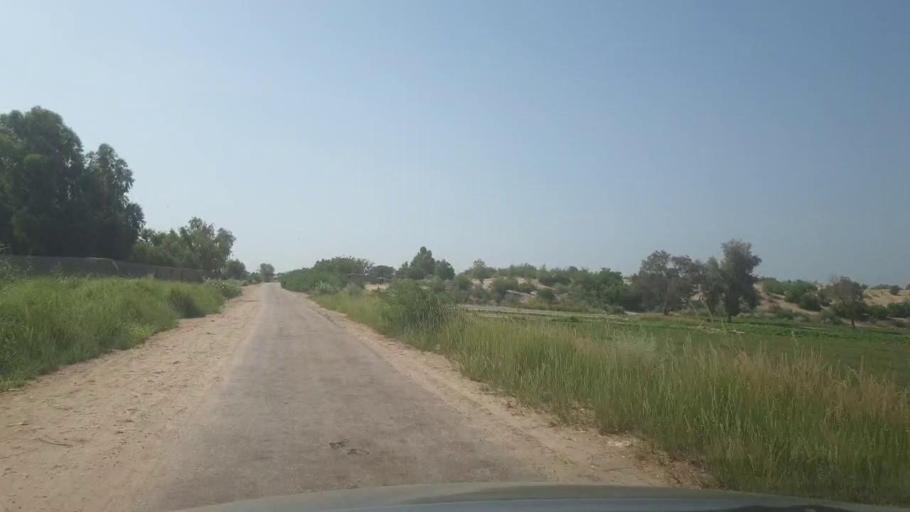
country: PK
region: Sindh
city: Rohri
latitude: 27.4314
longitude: 69.0768
